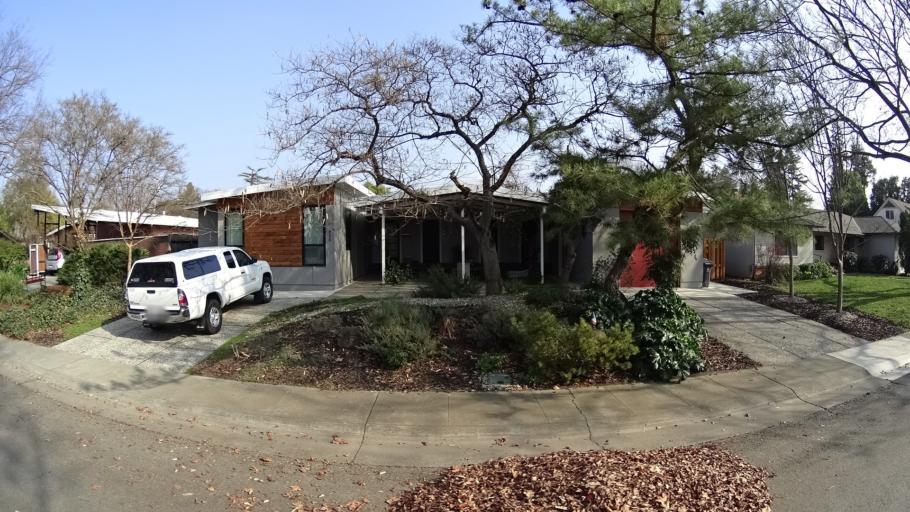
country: US
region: California
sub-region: Yolo County
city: Davis
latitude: 38.5491
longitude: -121.7555
